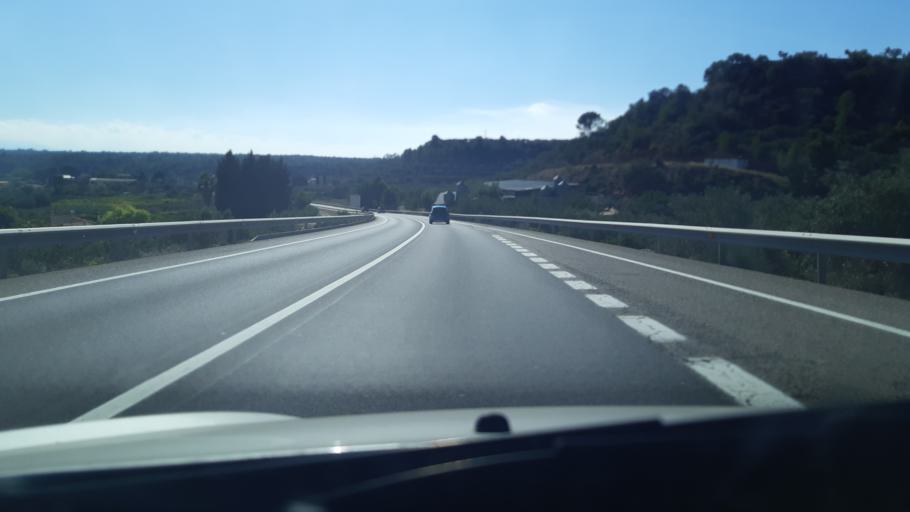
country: ES
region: Catalonia
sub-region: Provincia de Tarragona
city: Tivenys
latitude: 40.9107
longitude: 0.4840
